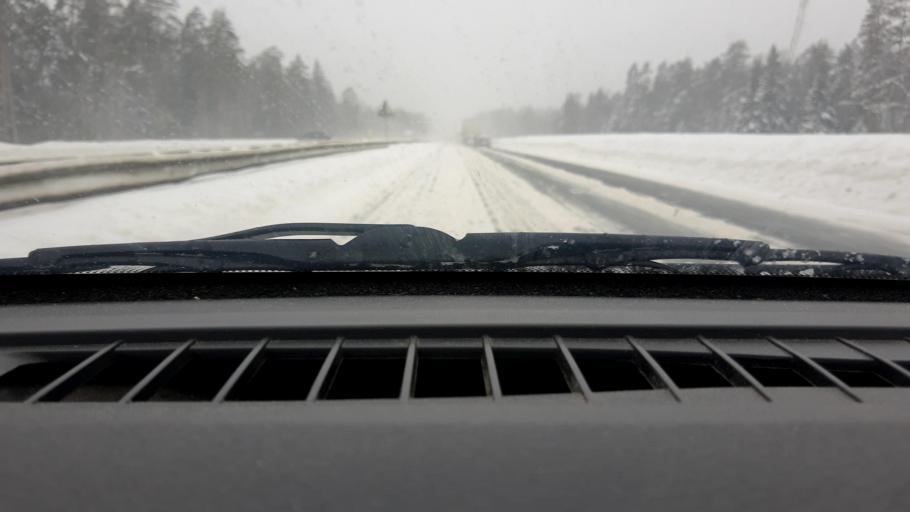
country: RU
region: Vladimir
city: Krasnyy Oktyabr'
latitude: 56.2177
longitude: 41.4455
